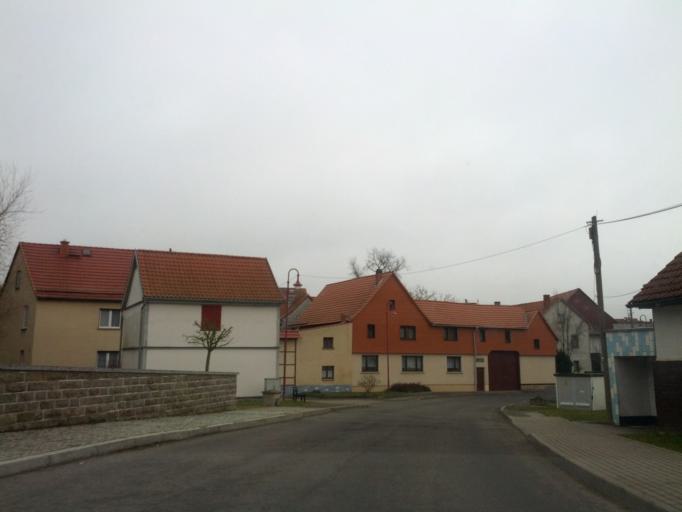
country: DE
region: Thuringia
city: Sonneborn
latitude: 51.0369
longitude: 10.5826
